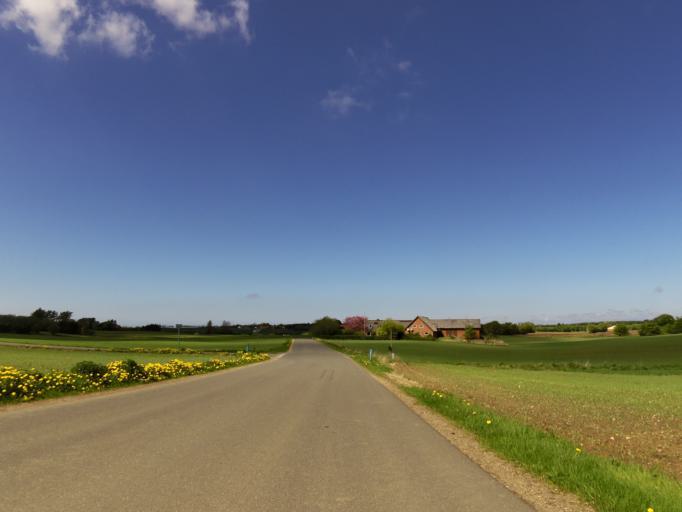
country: DK
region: Central Jutland
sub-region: Holstebro Kommune
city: Vinderup
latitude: 56.4231
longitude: 8.7833
